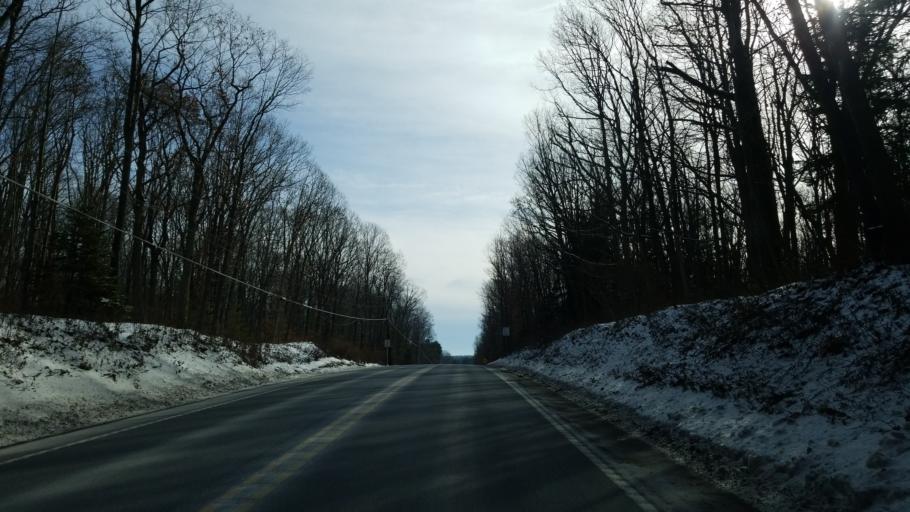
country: US
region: Pennsylvania
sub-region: Clearfield County
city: Clearfield
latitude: 41.1316
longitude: -78.5378
